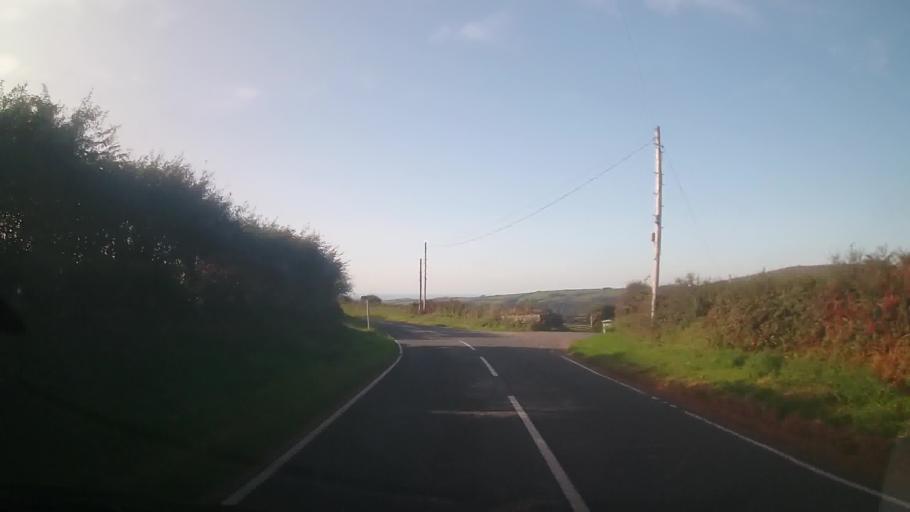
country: GB
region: Wales
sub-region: Pembrokeshire
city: Ambleston
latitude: 51.9693
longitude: -4.9056
